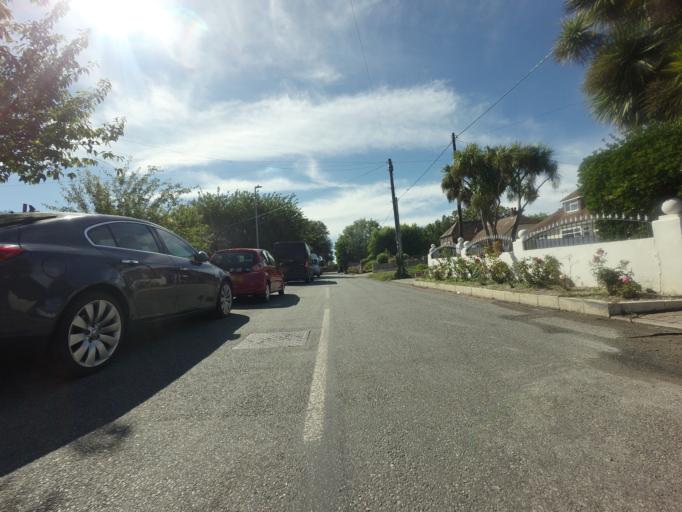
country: GB
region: England
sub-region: Kent
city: Birchington-on-Sea
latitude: 51.3380
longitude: 1.2850
